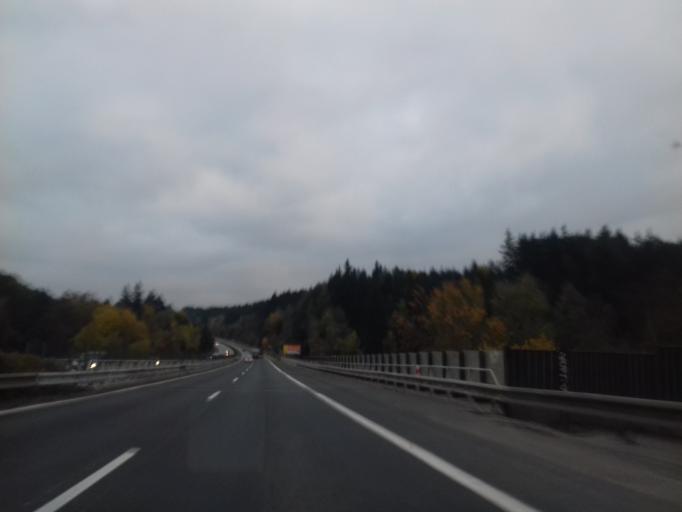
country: CZ
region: Central Bohemia
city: Divisov
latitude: 49.8177
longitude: 14.8757
